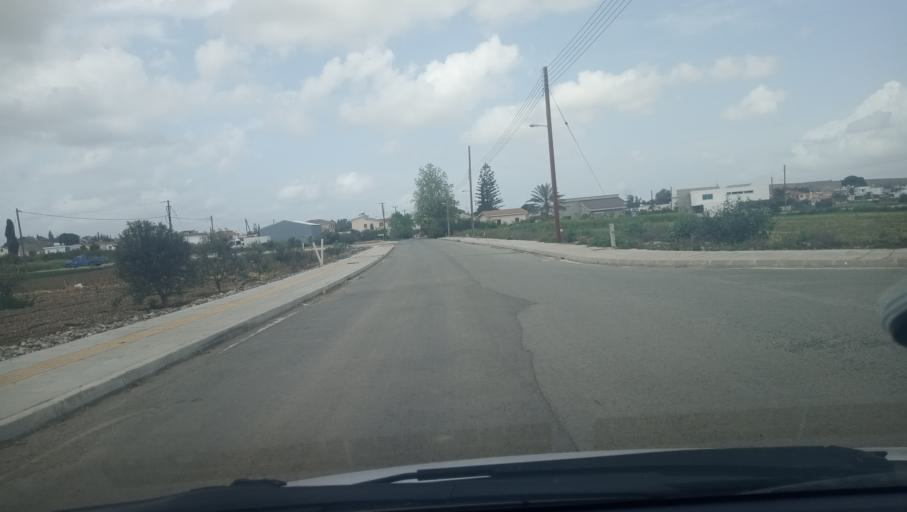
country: CY
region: Lefkosia
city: Pano Deftera
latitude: 35.0739
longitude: 33.2675
